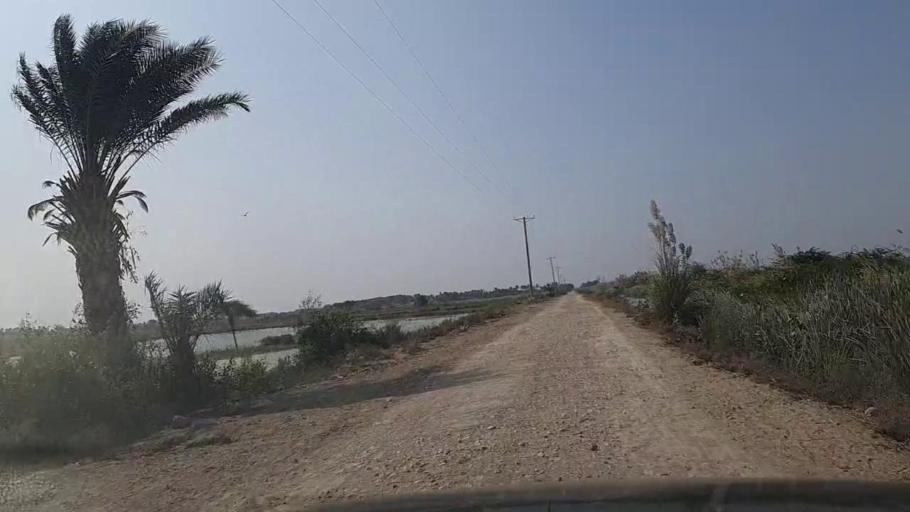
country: PK
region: Sindh
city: Gharo
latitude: 24.6830
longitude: 67.5997
